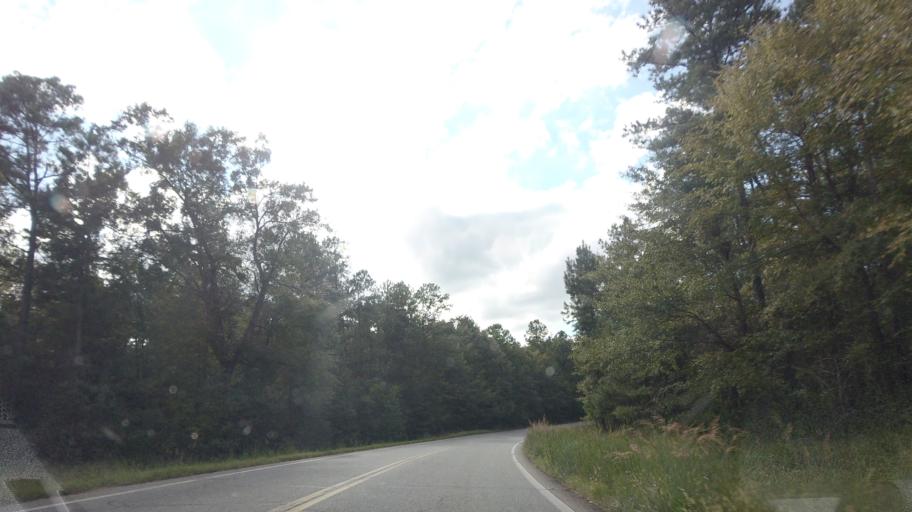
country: US
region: Georgia
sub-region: Monroe County
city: Forsyth
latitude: 33.0276
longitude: -83.7827
